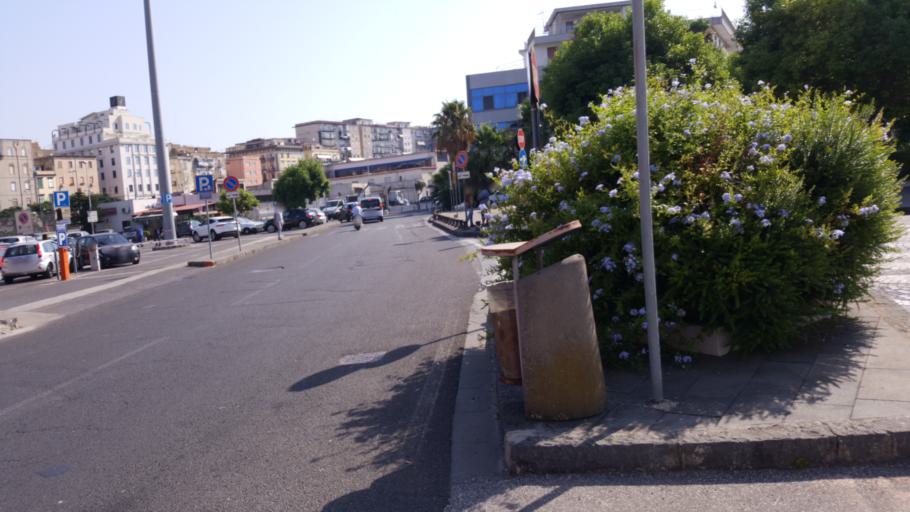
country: IT
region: Campania
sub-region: Provincia di Napoli
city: Napoli
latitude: 40.8444
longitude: 14.2624
